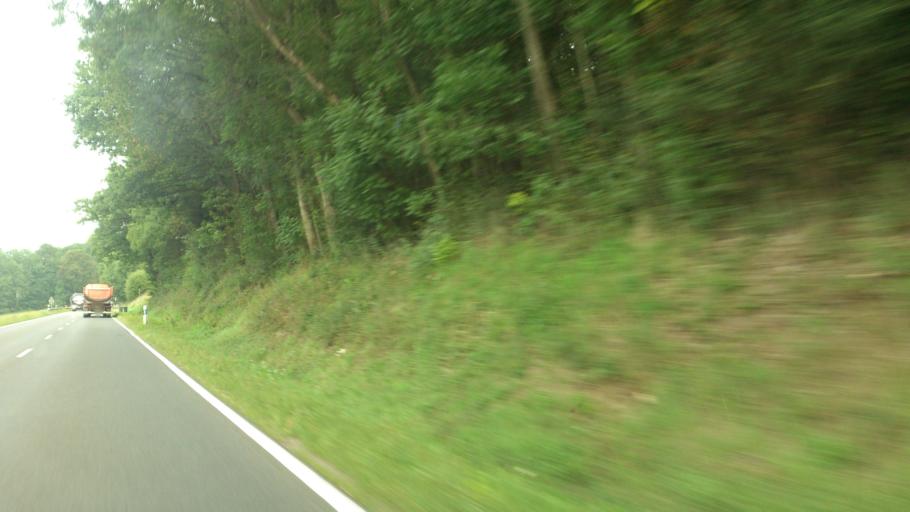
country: DE
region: Rheinland-Pfalz
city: Uxheim
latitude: 50.3850
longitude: 6.7541
